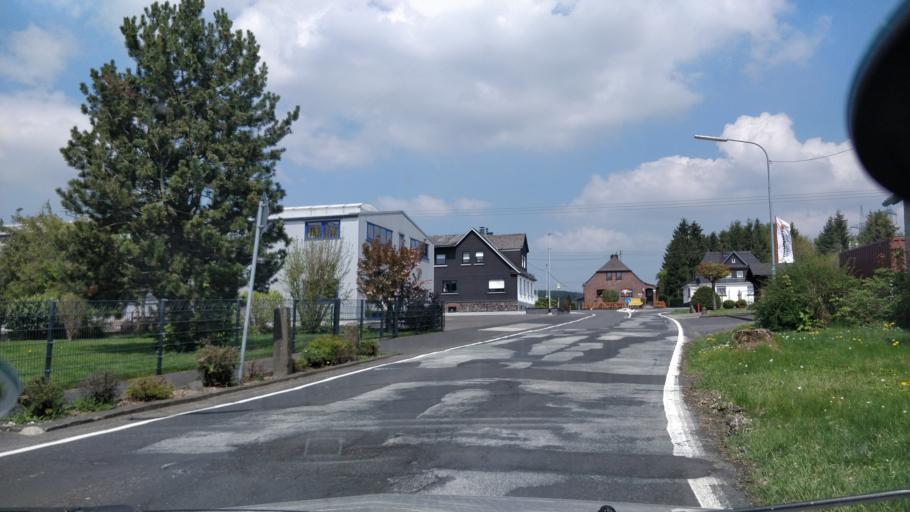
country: DE
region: Rheinland-Pfalz
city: Fehl-Ritzhausen
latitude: 50.6424
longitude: 8.0068
